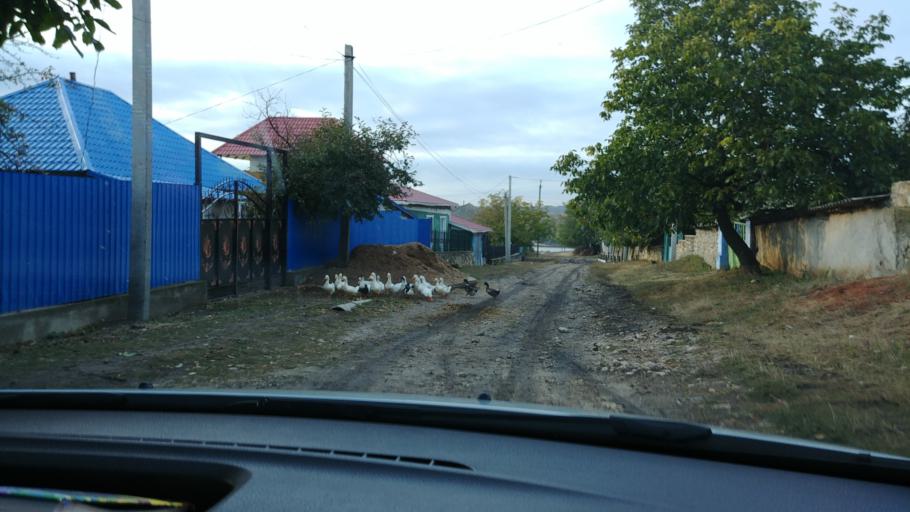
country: MD
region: Rezina
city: Saharna
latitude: 47.6784
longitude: 28.9589
